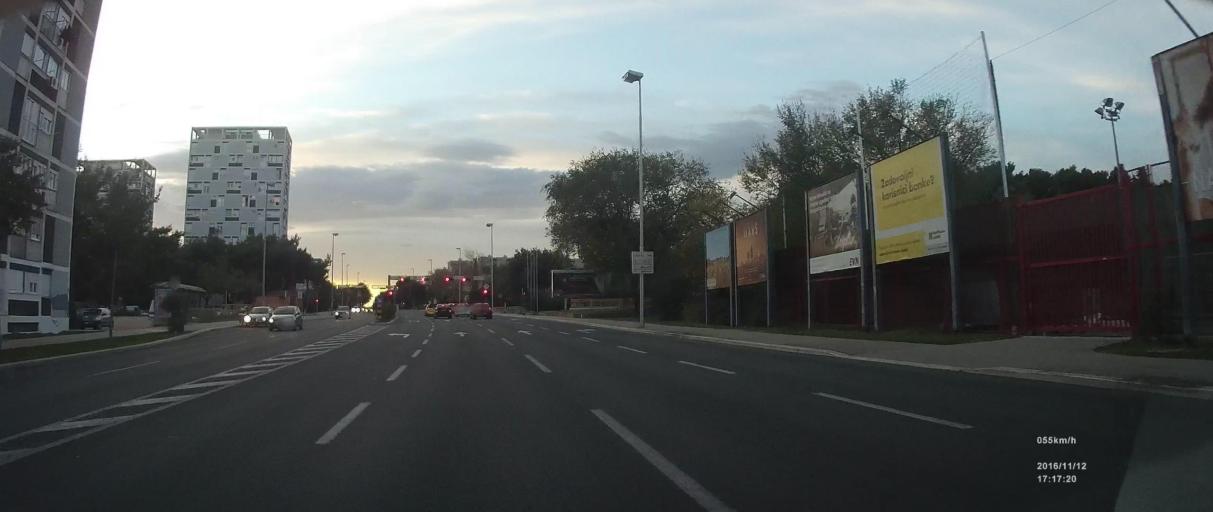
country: HR
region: Splitsko-Dalmatinska
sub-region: Grad Split
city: Split
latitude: 43.5185
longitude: 16.4415
